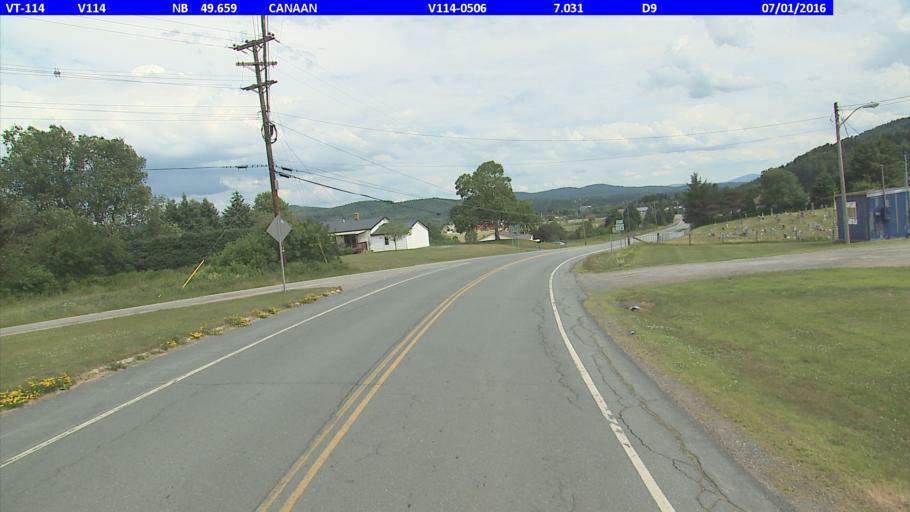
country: US
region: New Hampshire
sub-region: Coos County
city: Colebrook
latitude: 45.0069
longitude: -71.5559
